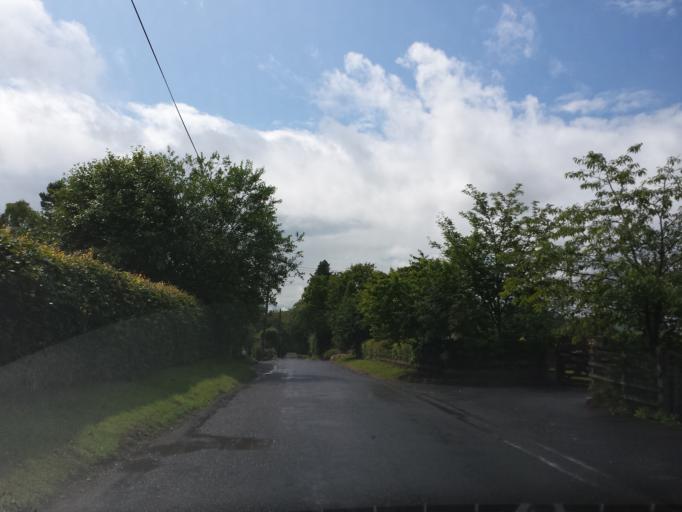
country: GB
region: Scotland
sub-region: The Scottish Borders
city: Saint Boswells
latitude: 55.5946
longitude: -2.6425
